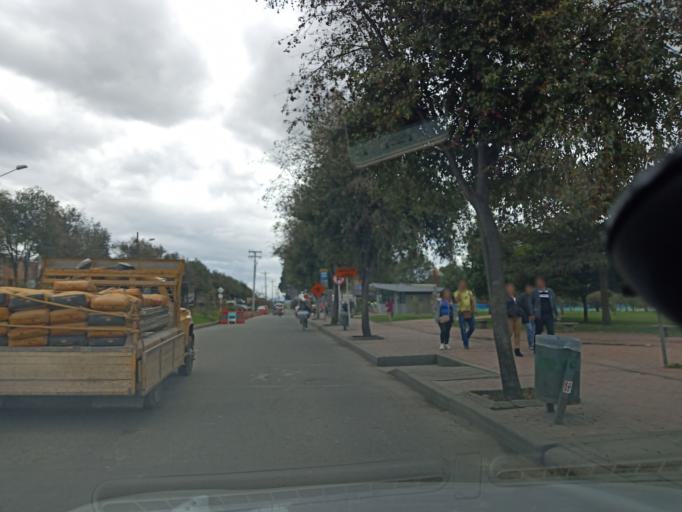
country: CO
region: Cundinamarca
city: Funza
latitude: 4.6710
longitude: -74.1561
